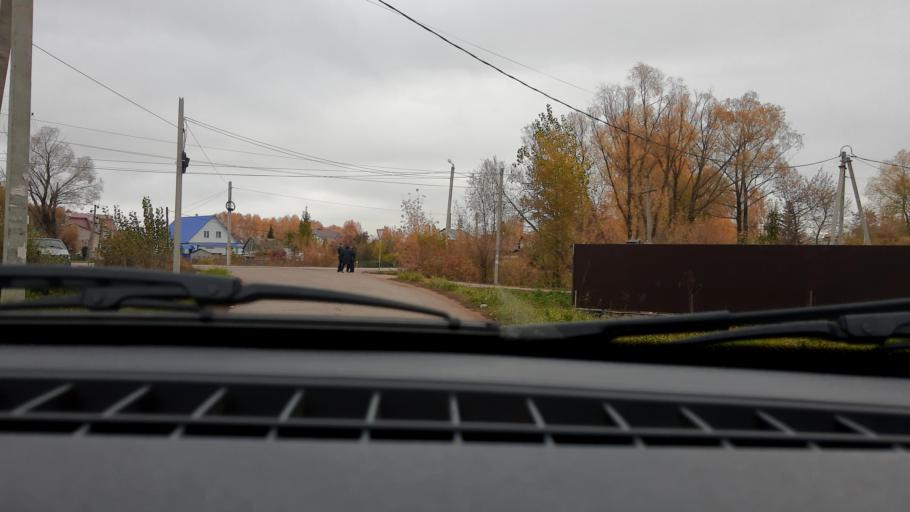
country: RU
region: Bashkortostan
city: Mikhaylovka
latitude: 54.7804
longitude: 55.8309
